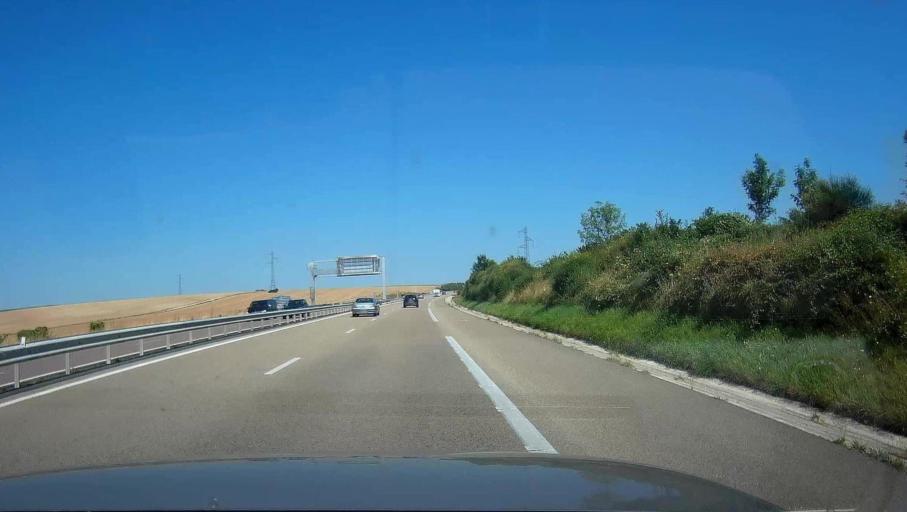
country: FR
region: Champagne-Ardenne
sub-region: Departement de l'Aube
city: Creney-pres-Troyes
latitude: 48.3150
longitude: 4.1640
